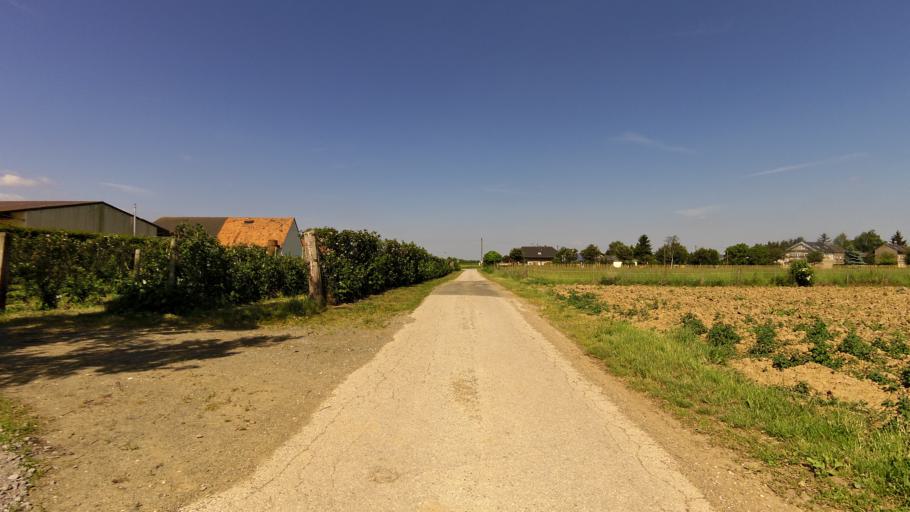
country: DE
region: North Rhine-Westphalia
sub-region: Regierungsbezirk Koln
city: Rheinbach
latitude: 50.6396
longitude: 6.9645
